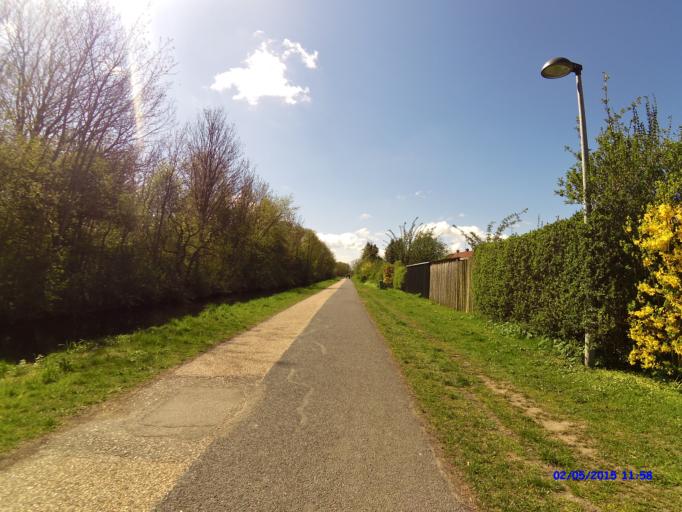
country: DK
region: Capital Region
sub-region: Gladsaxe Municipality
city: Buddinge
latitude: 55.7254
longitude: 12.5171
